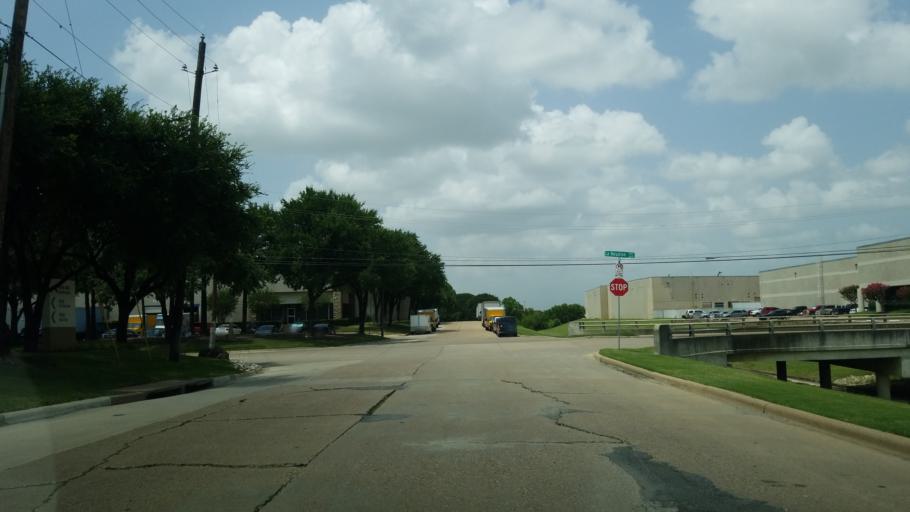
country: US
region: Texas
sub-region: Dallas County
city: Cockrell Hill
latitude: 32.7707
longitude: -96.8916
